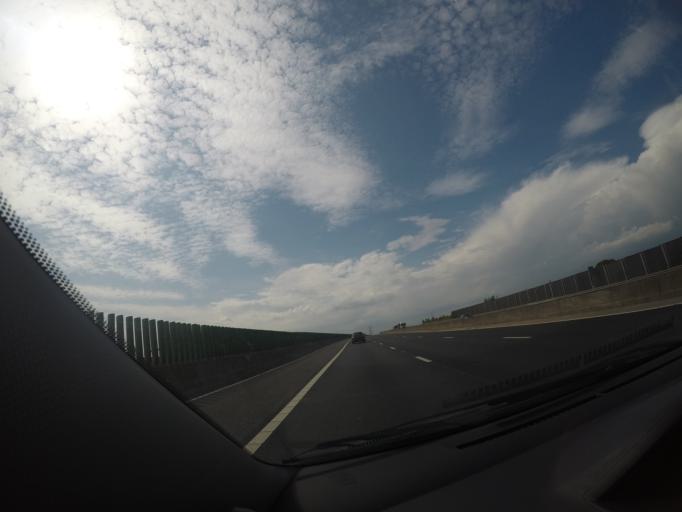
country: GB
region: Scotland
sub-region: Dumfries and Galloway
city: Gretna
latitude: 54.9791
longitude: -3.0208
